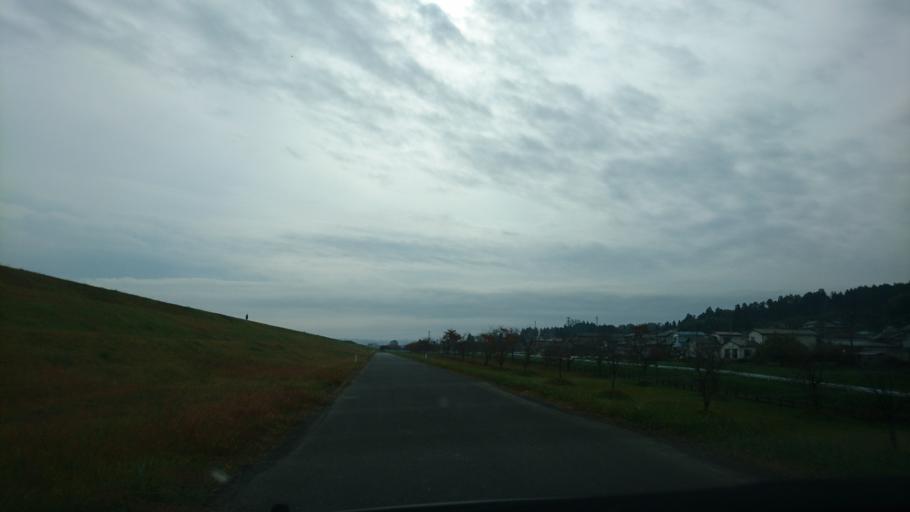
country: JP
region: Iwate
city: Ichinoseki
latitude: 38.9589
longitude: 141.1299
